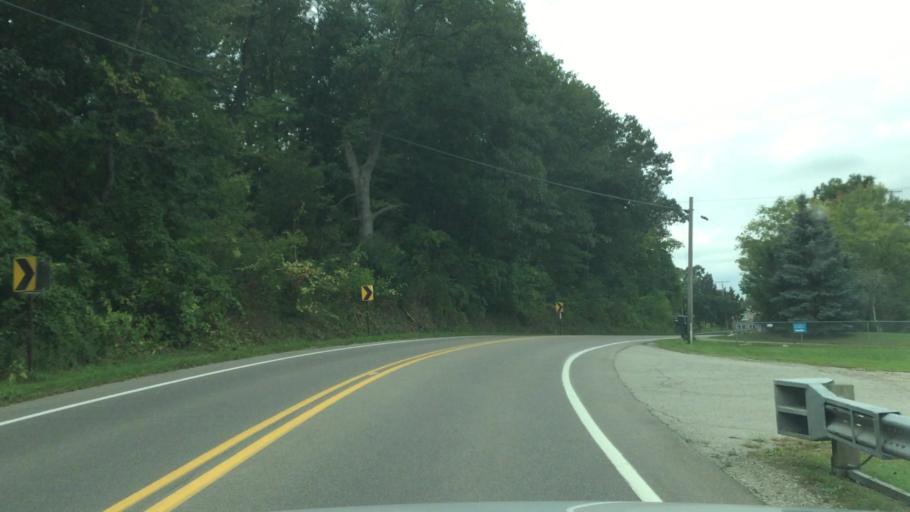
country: US
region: Michigan
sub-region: Livingston County
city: Brighton
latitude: 42.5503
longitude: -83.7746
